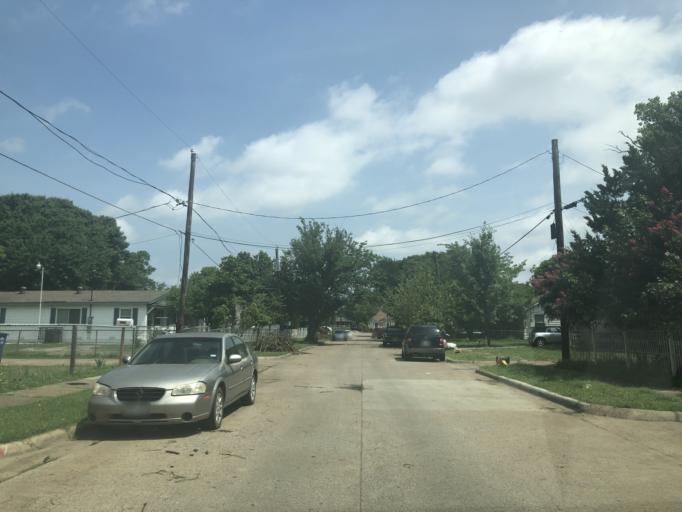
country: US
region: Texas
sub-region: Dallas County
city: Cockrell Hill
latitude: 32.7909
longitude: -96.8782
